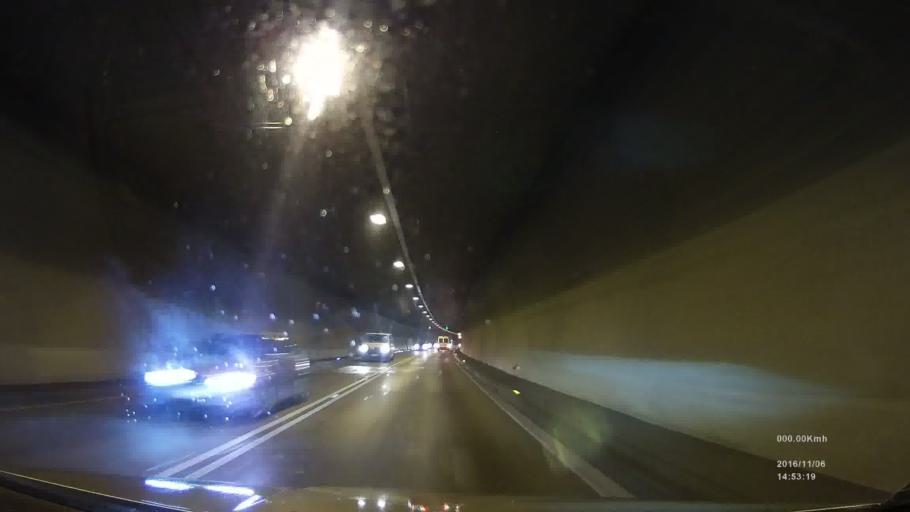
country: SK
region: Kosicky
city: Krompachy
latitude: 49.0076
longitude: 20.8581
